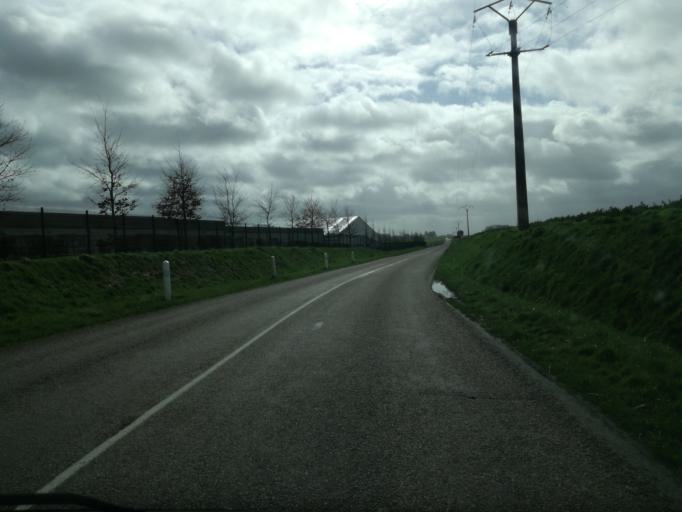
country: FR
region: Haute-Normandie
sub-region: Departement de la Seine-Maritime
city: Valliquerville
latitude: 49.6097
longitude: 0.6659
